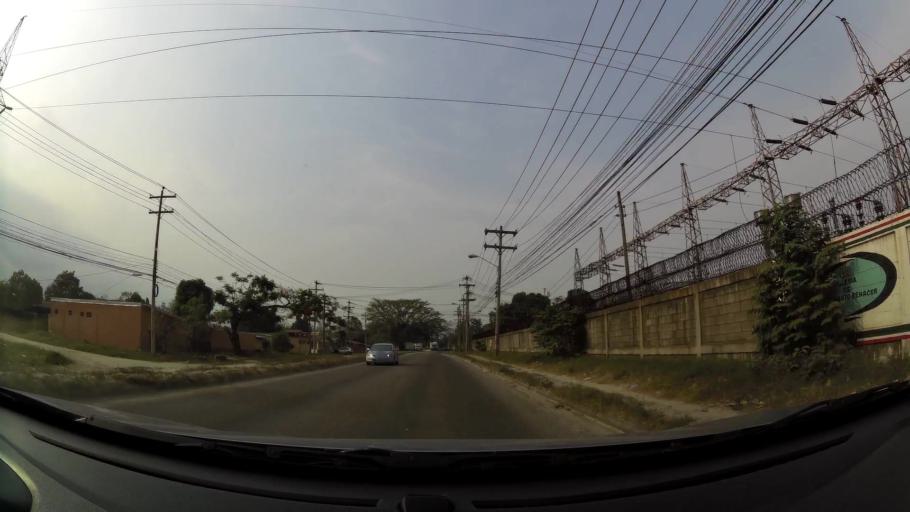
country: HN
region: Cortes
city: San Pedro Sula
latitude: 15.5338
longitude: -88.0137
